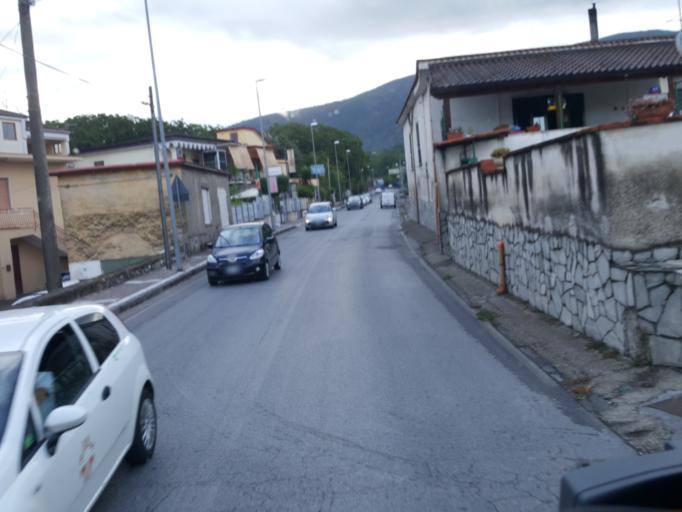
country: IT
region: Campania
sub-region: Provincia di Napoli
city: Palma Campania
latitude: 40.8786
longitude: 14.5578
